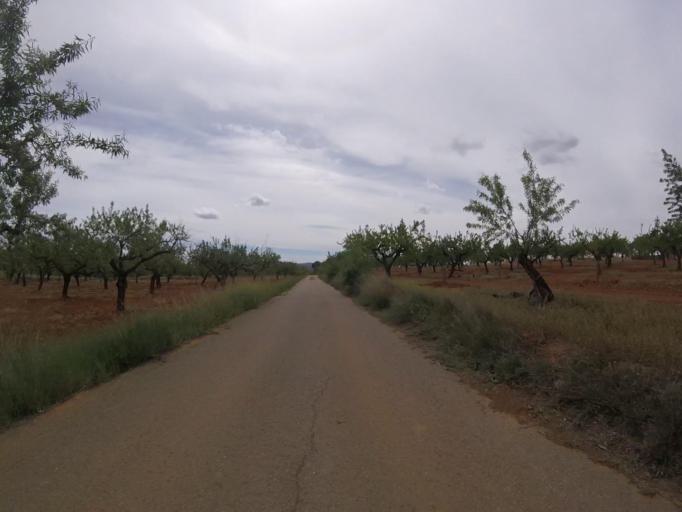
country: ES
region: Valencia
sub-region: Provincia de Castello
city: Benlloch
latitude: 40.1838
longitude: -0.0087
